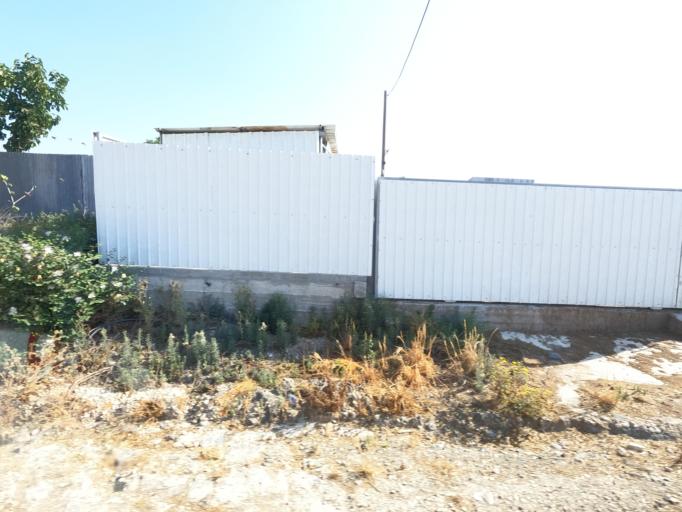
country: CY
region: Lefkosia
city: Lympia
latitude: 34.9870
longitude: 33.4751
